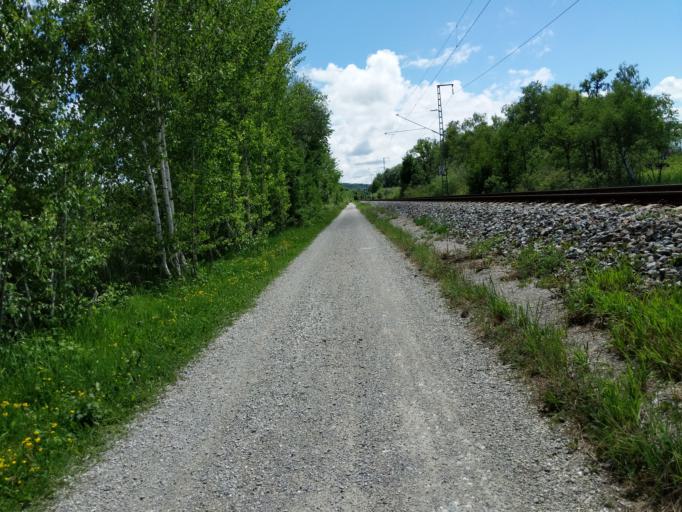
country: DE
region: Bavaria
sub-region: Upper Bavaria
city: Herrsching am Ammersee
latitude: 48.0105
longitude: 11.1726
